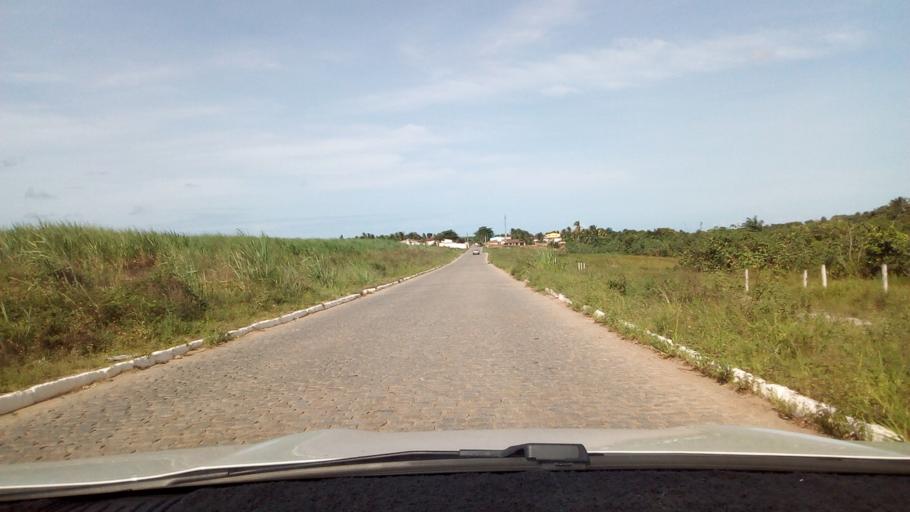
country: BR
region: Paraiba
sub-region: Santa Rita
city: Santa Rita
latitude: -7.0818
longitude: -34.9668
